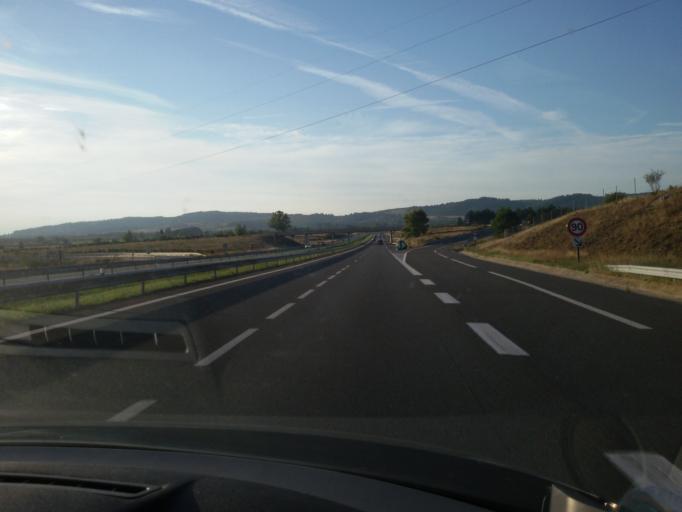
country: FR
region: Midi-Pyrenees
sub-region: Departement de l'Aveyron
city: La Cavalerie
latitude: 43.9487
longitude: 3.2184
